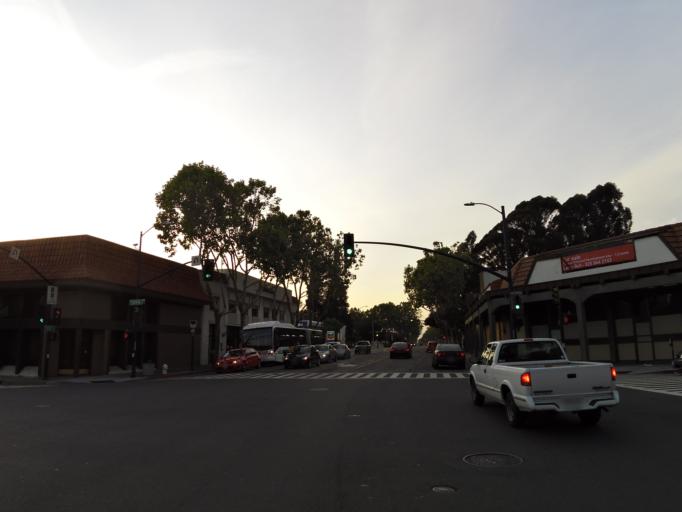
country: US
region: California
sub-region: Alameda County
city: San Leandro
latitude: 37.7257
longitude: -122.1568
